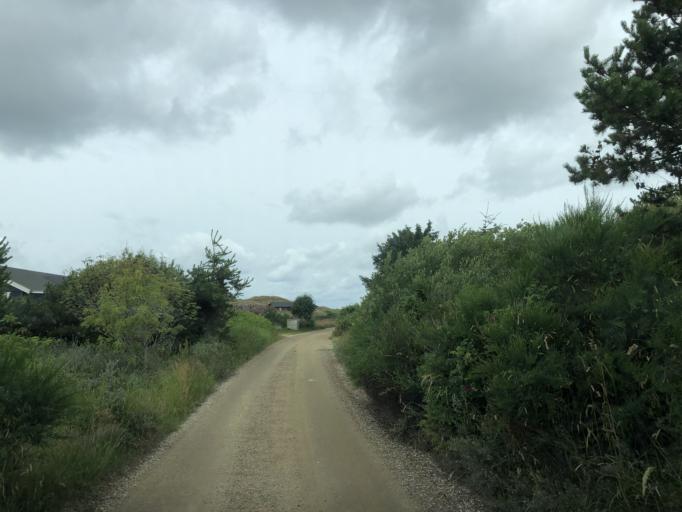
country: DK
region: Central Jutland
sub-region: Ringkobing-Skjern Kommune
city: Hvide Sande
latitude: 55.9233
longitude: 8.1695
